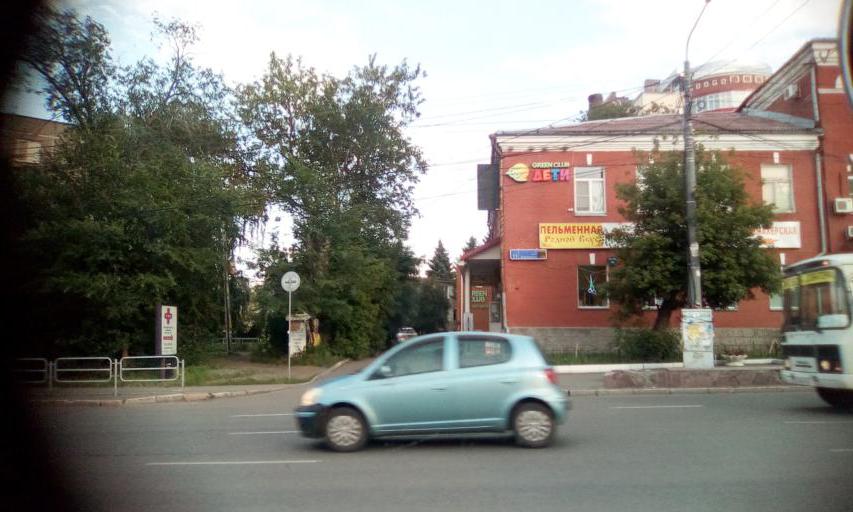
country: RU
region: Chelyabinsk
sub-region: Gorod Chelyabinsk
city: Chelyabinsk
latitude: 55.1556
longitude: 61.3948
